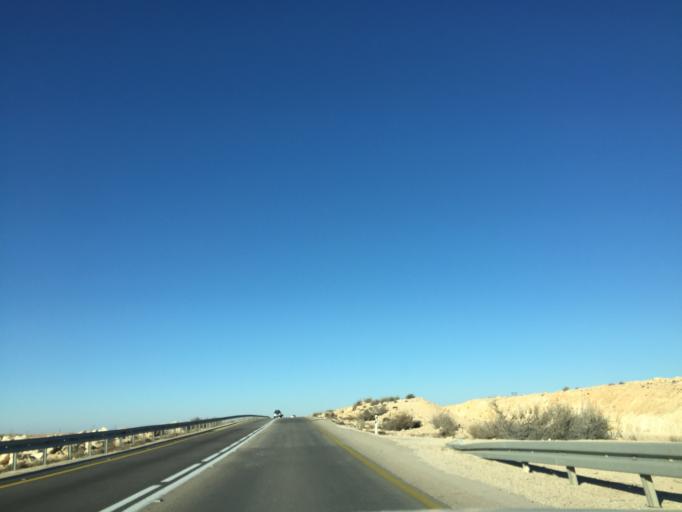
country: IL
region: Southern District
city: Mitzpe Ramon
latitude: 30.6417
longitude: 34.8068
